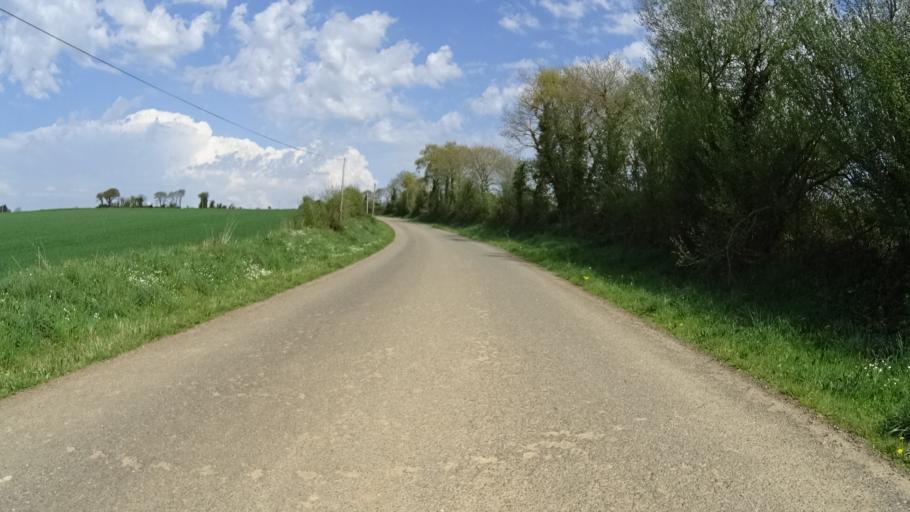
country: FR
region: Brittany
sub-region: Departement du Finistere
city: Sizun
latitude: 48.4263
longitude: -4.0827
